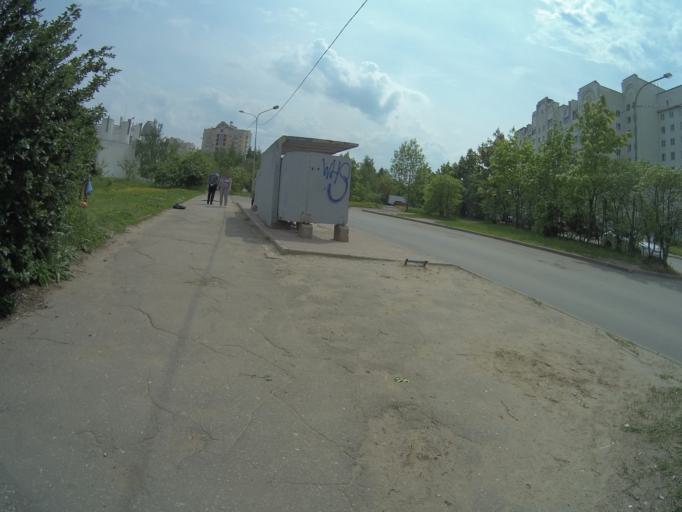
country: RU
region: Vladimir
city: Vladimir
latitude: 56.1354
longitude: 40.3780
